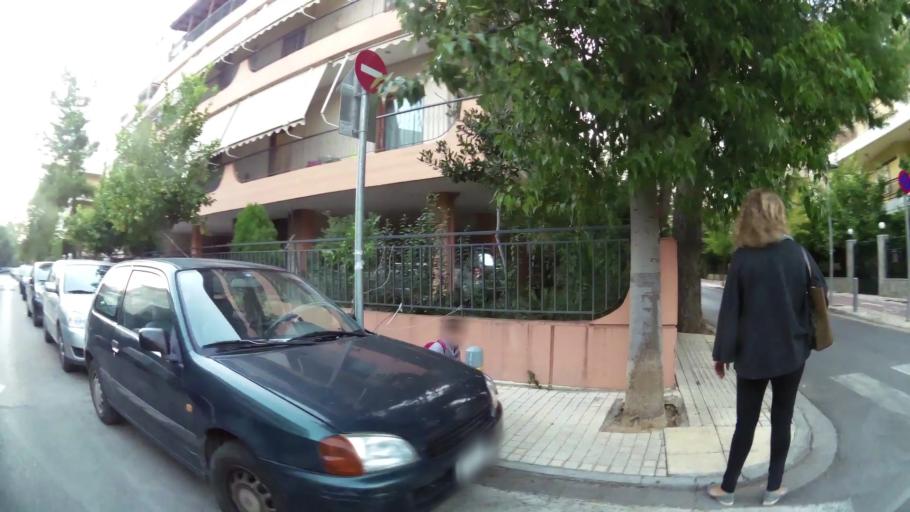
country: GR
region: Attica
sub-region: Nomarchia Athinas
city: Agia Paraskevi
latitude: 38.0215
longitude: 23.8340
